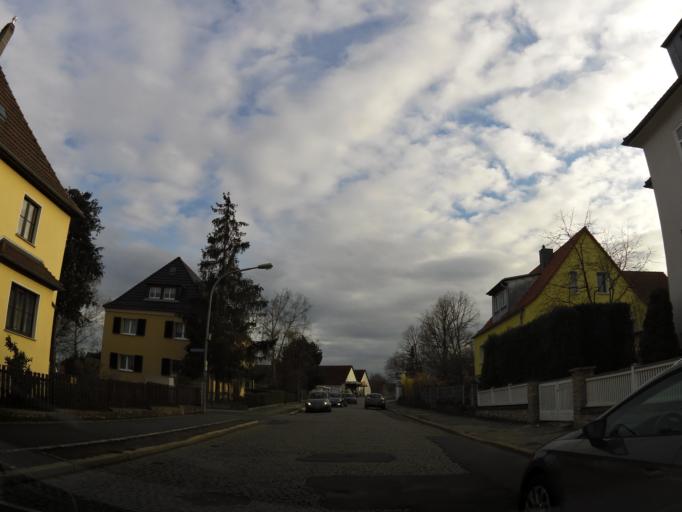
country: DE
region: Thuringia
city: Weimar
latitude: 50.9673
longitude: 11.3286
